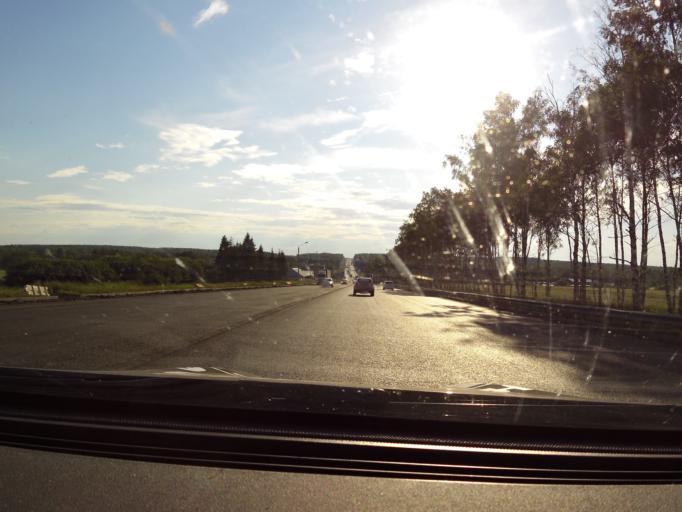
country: RU
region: Vladimir
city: Melekhovo
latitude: 56.2127
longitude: 41.3362
